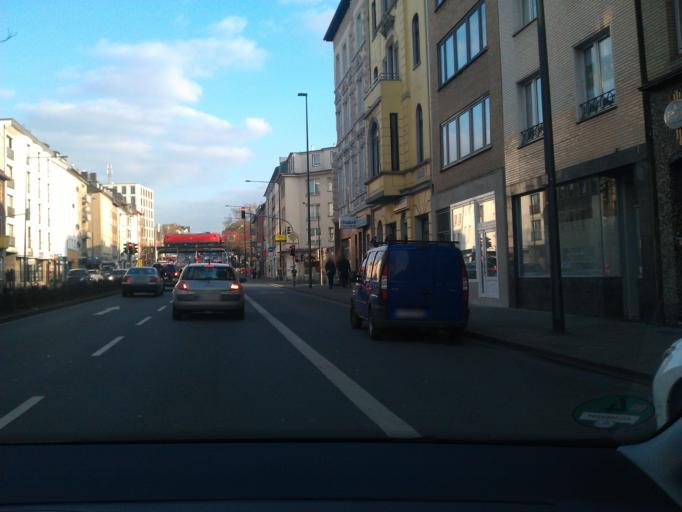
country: DE
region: North Rhine-Westphalia
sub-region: Regierungsbezirk Koln
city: Aachen
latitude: 50.7718
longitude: 6.1140
